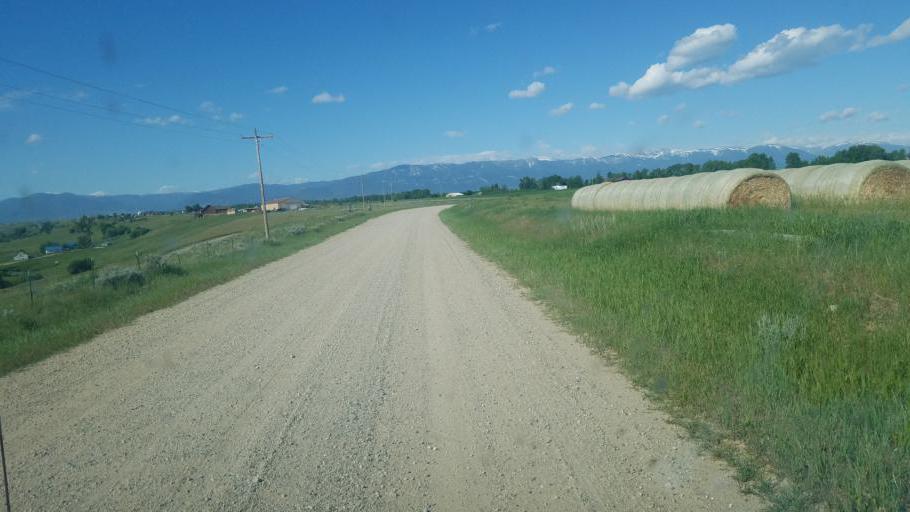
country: US
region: Montana
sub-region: Carbon County
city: Red Lodge
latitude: 45.3292
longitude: -109.1685
